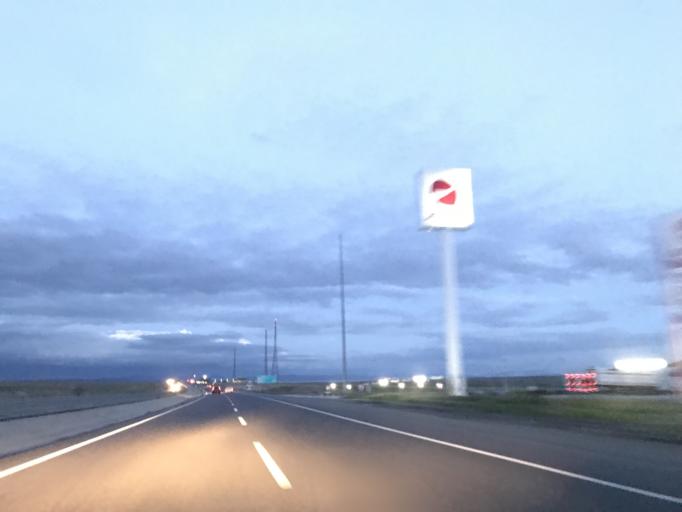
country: TR
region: Konya
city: Kulu
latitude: 39.1581
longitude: 33.2032
